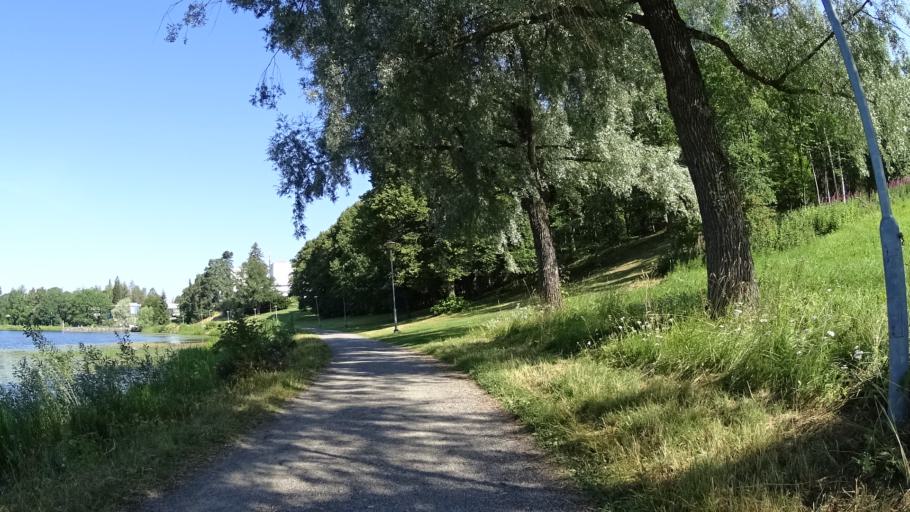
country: FI
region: Haeme
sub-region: Haemeenlinna
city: Haemeenlinna
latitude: 61.0202
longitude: 24.4472
